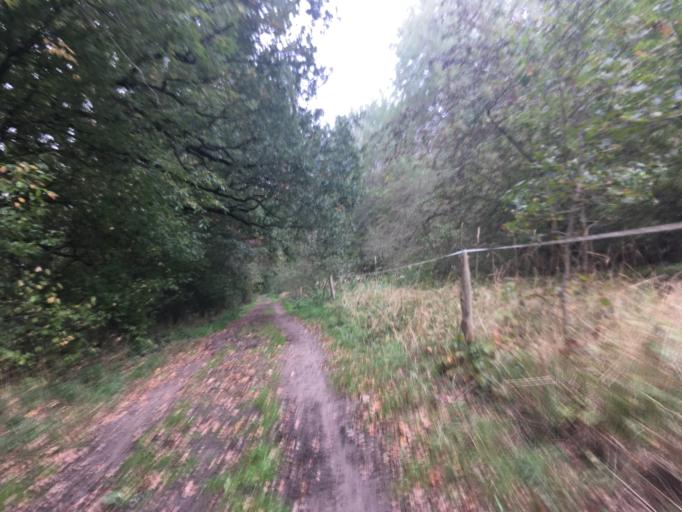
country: DE
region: Brandenburg
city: Falkensee
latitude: 52.5205
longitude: 13.0974
